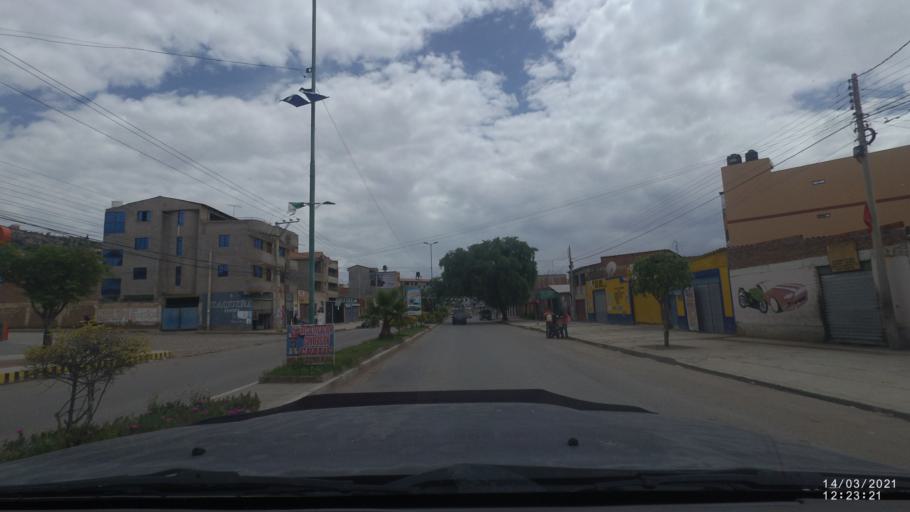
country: BO
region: Cochabamba
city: Cochabamba
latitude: -17.4246
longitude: -66.1334
